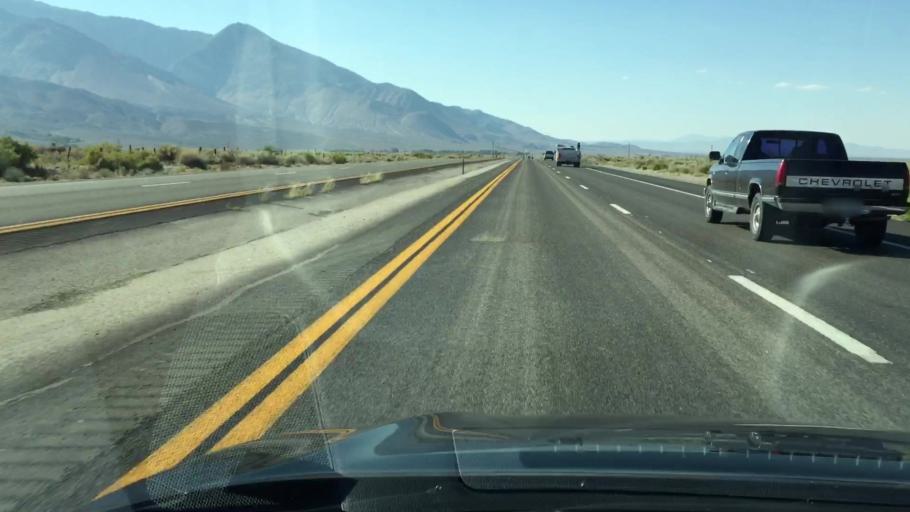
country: US
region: California
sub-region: Inyo County
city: Big Pine
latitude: 37.1925
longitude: -118.3089
